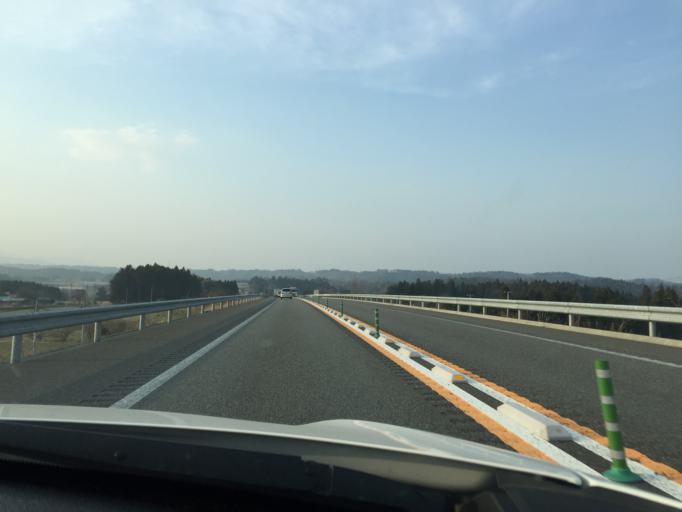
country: JP
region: Fukushima
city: Namie
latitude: 37.5669
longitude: 140.9445
